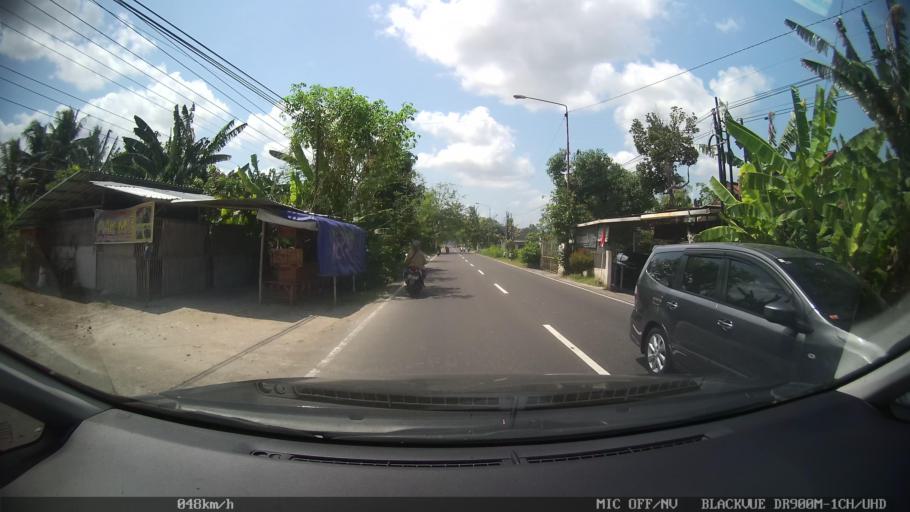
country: ID
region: Daerah Istimewa Yogyakarta
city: Bantul
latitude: -7.9048
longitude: 110.3279
